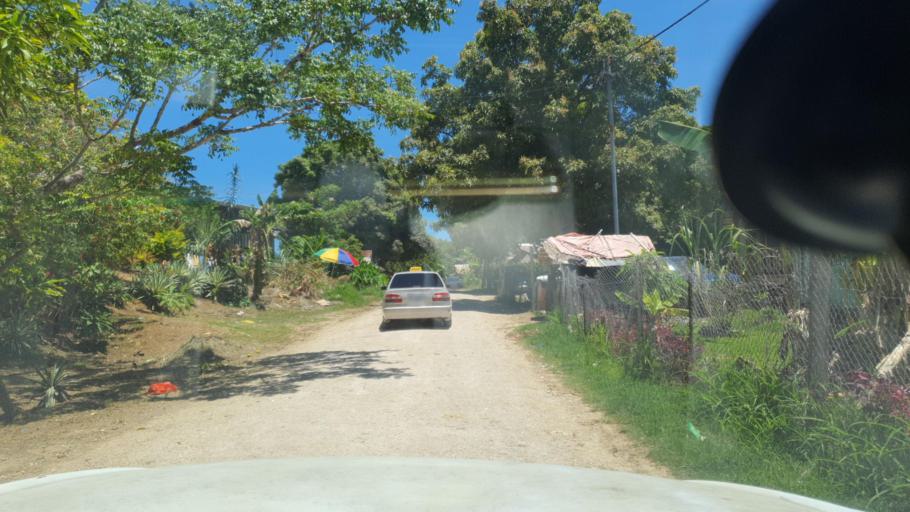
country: SB
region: Guadalcanal
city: Honiara
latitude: -9.4539
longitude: 159.9890
